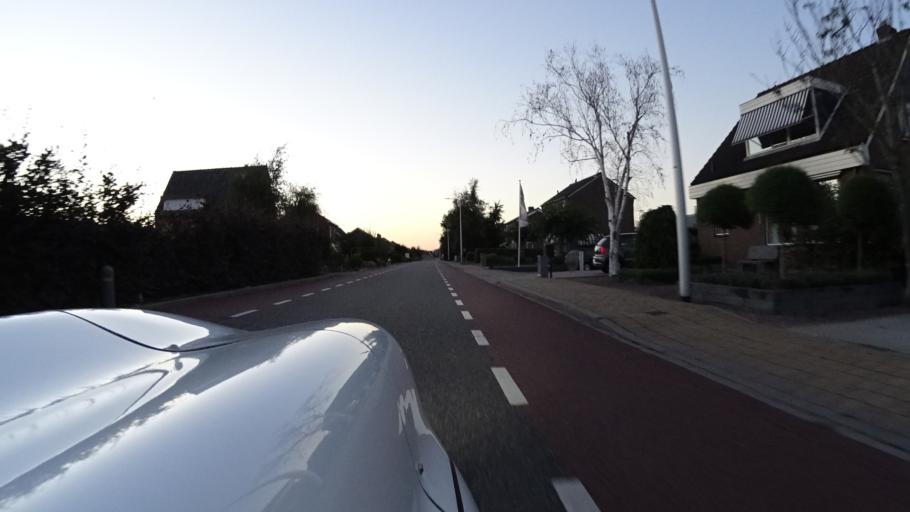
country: NL
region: South Holland
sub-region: Gemeente Kaag en Braassem
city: Oude Wetering
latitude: 52.1906
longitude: 4.6203
